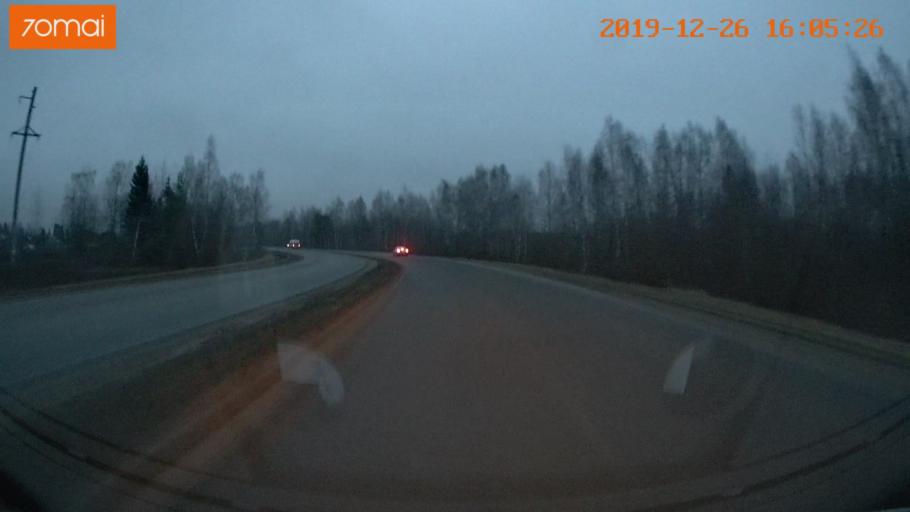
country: RU
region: Jaroslavl
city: Rybinsk
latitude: 58.0056
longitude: 38.8958
